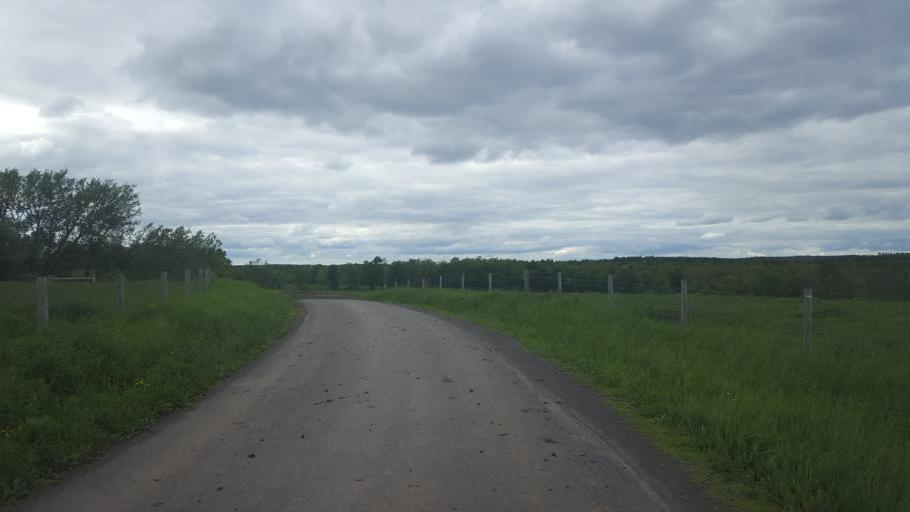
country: US
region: New York
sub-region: Otsego County
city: Richfield Springs
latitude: 42.8530
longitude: -74.9445
